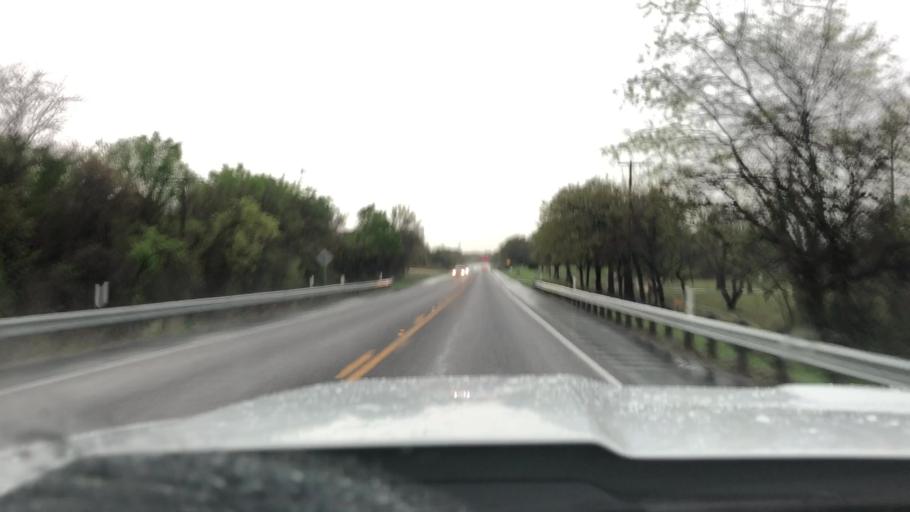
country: US
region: Texas
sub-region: Johnson County
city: Keene
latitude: 32.4129
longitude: -97.3225
